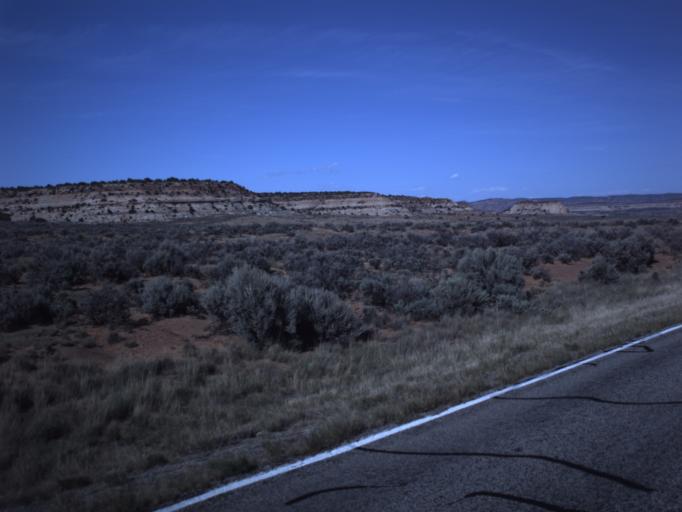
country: US
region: Utah
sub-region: San Juan County
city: Monticello
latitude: 38.0619
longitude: -109.3962
